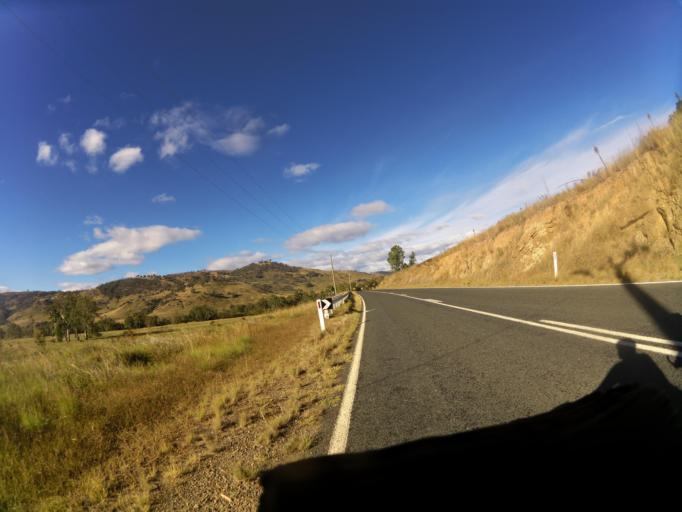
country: AU
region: New South Wales
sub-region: Greater Hume Shire
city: Holbrook
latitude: -35.9655
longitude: 147.7622
